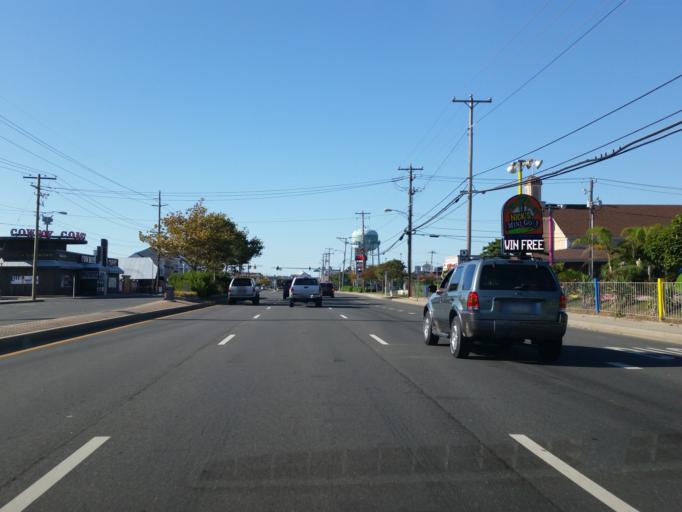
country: US
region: Maryland
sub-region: Worcester County
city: Ocean City
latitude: 38.3487
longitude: -75.0787
